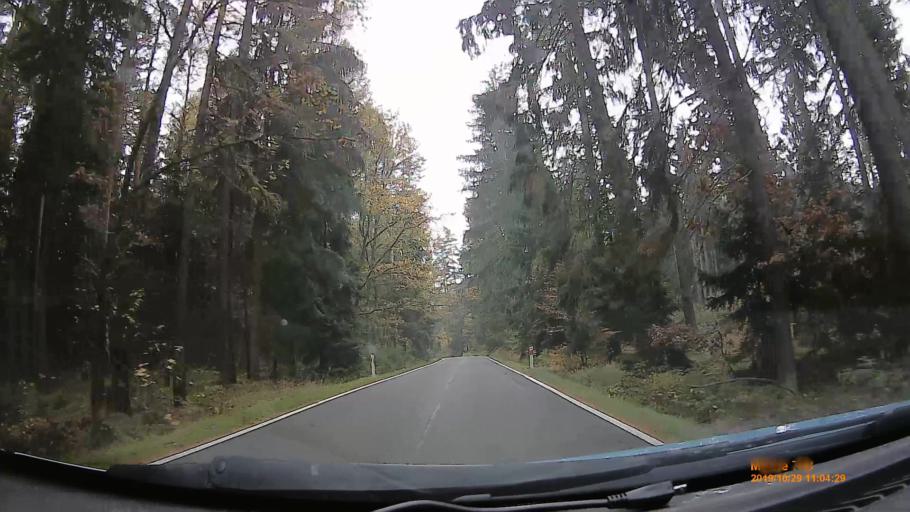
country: PL
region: Lower Silesian Voivodeship
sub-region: Powiat klodzki
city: Szczytna
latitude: 50.4770
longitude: 16.4658
